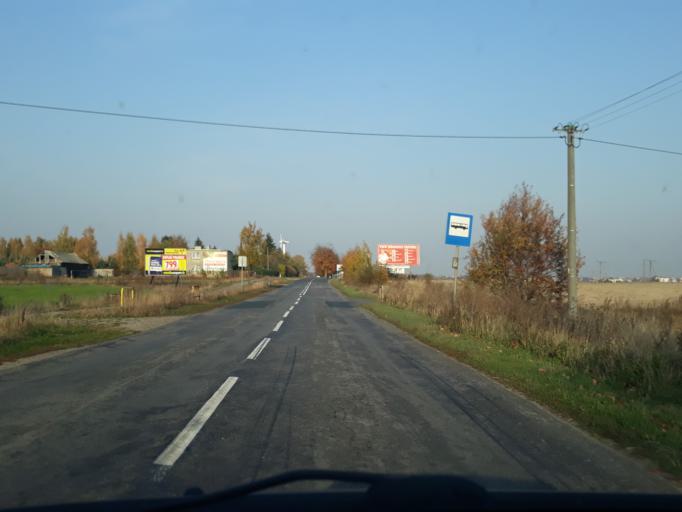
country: PL
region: Pomeranian Voivodeship
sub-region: Powiat chojnicki
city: Chojnice
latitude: 53.6779
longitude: 17.5359
